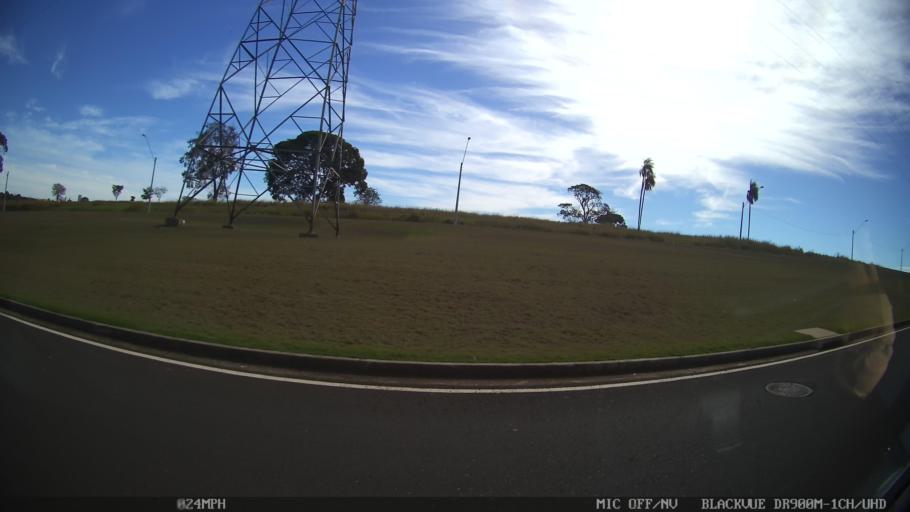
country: BR
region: Sao Paulo
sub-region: Sao Jose Do Rio Preto
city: Sao Jose do Rio Preto
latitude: -20.8576
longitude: -49.3794
